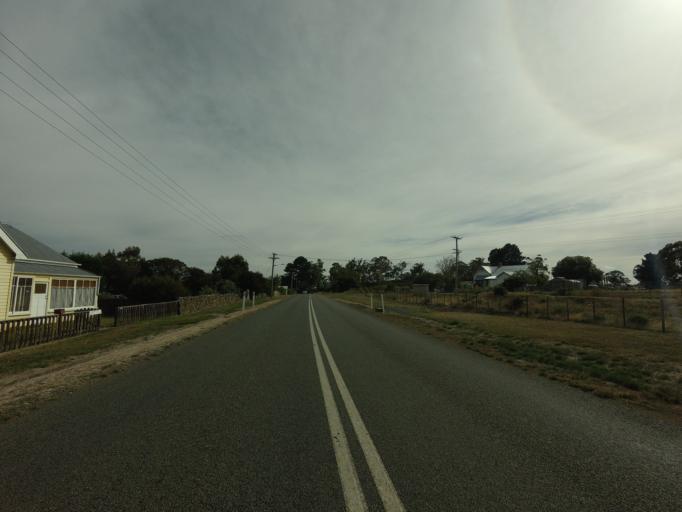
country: AU
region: Tasmania
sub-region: Brighton
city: Bridgewater
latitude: -42.3561
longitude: 147.4068
